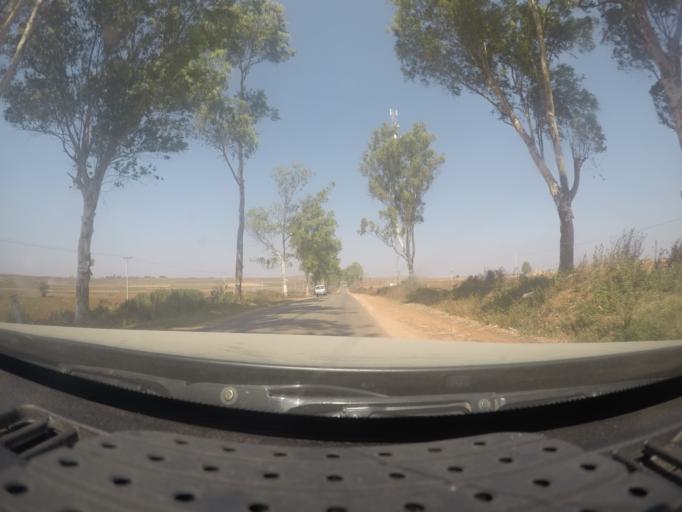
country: MM
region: Shan
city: Taunggyi
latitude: 20.7957
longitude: 96.6335
